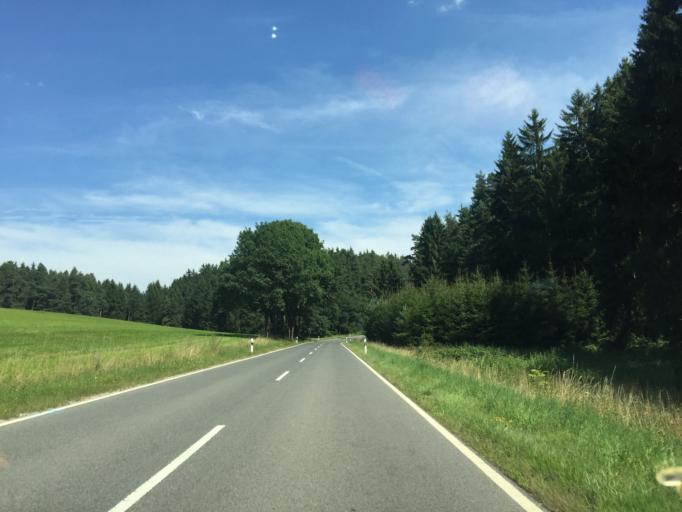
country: DE
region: Bavaria
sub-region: Upper Palatinate
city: Pressath
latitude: 49.7650
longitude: 11.9765
